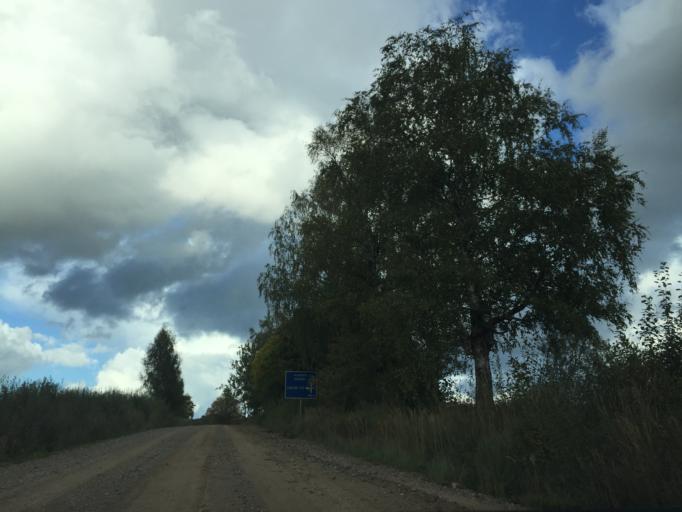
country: LV
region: Amatas Novads
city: Drabesi
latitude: 57.0626
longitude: 25.1757
